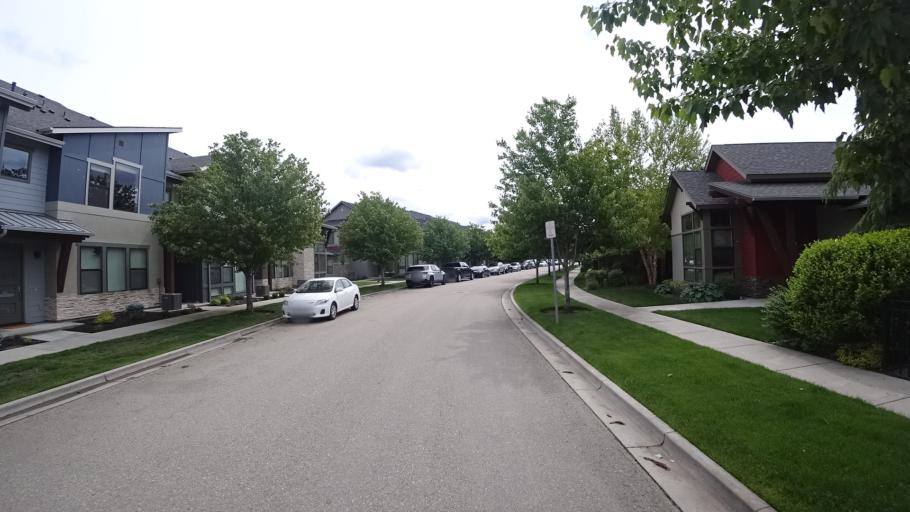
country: US
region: Idaho
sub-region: Ada County
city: Eagle
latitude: 43.6876
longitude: -116.3392
